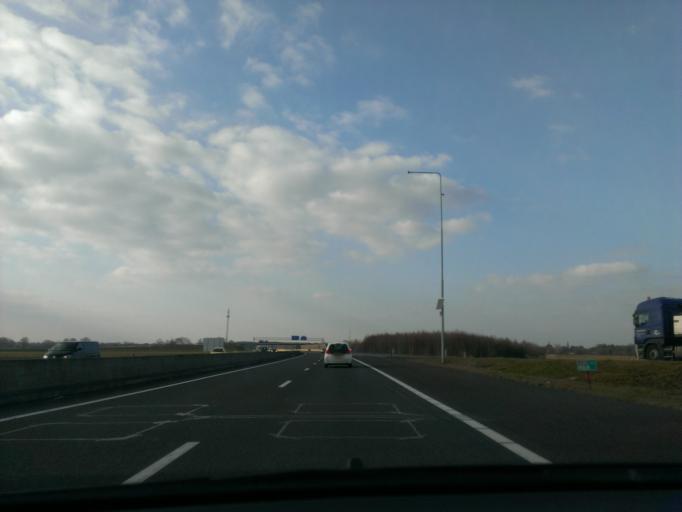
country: NL
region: Overijssel
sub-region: Gemeente Wierden
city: Wierden
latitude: 52.3435
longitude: 6.5956
